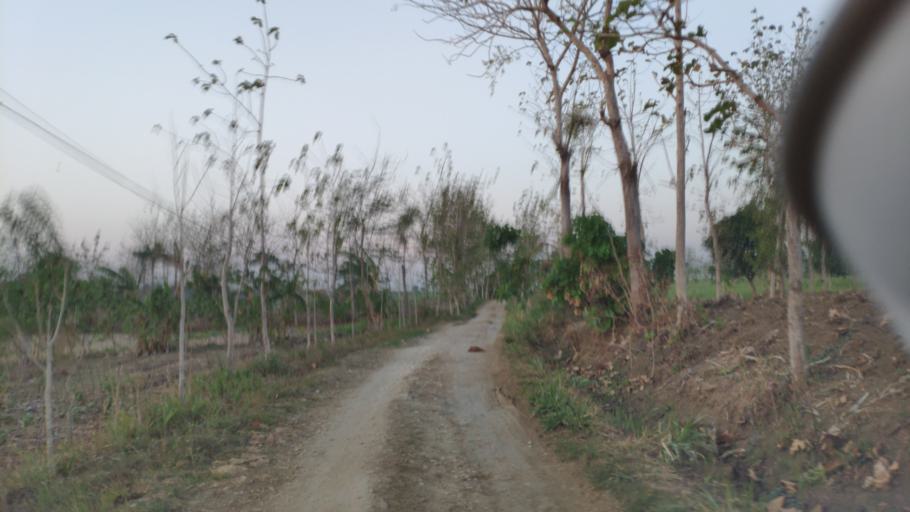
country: ID
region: Central Java
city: Jagong
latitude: -7.0383
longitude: 111.2394
